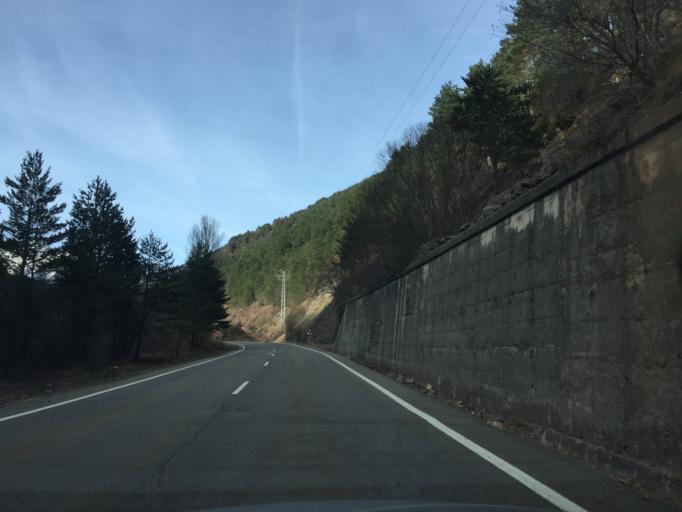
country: ES
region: Aragon
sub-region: Provincia de Huesca
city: Bielsa
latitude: 42.6074
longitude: 0.2389
